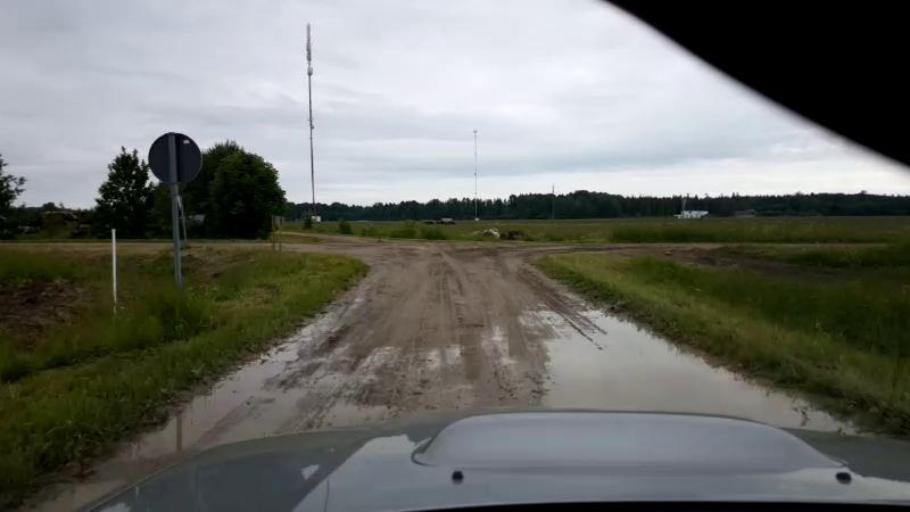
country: EE
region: Paernumaa
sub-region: Halinga vald
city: Parnu-Jaagupi
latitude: 58.5328
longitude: 24.5765
